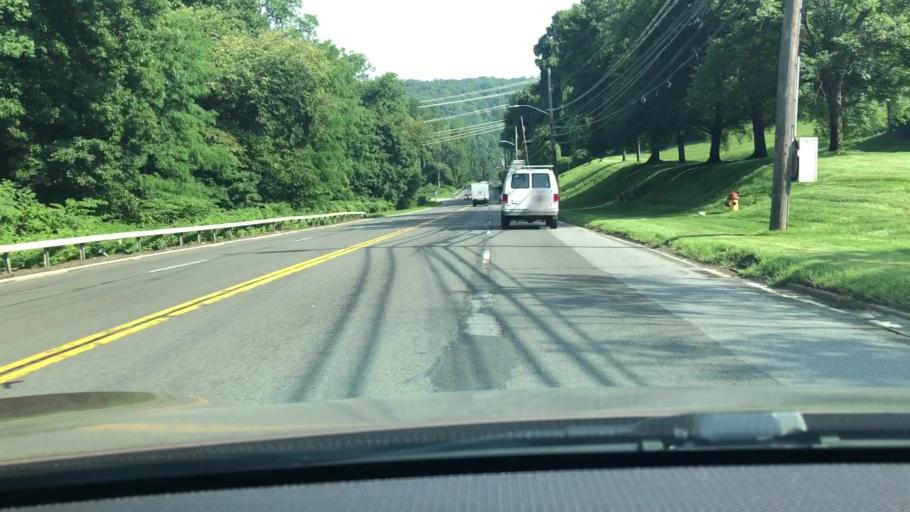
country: US
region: New York
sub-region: Westchester County
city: Elmsford
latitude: 41.0853
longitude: -73.8191
